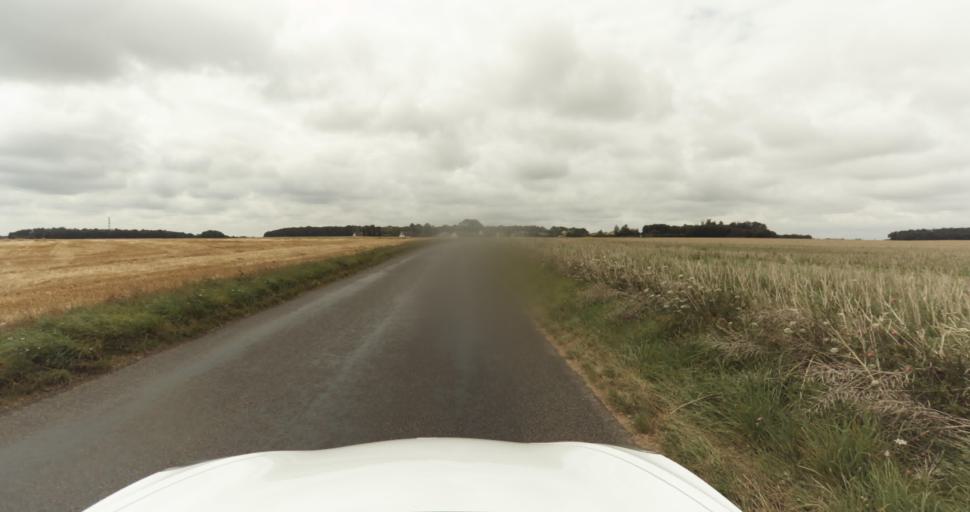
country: FR
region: Haute-Normandie
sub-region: Departement de l'Eure
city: Claville
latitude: 49.0312
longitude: 1.0525
